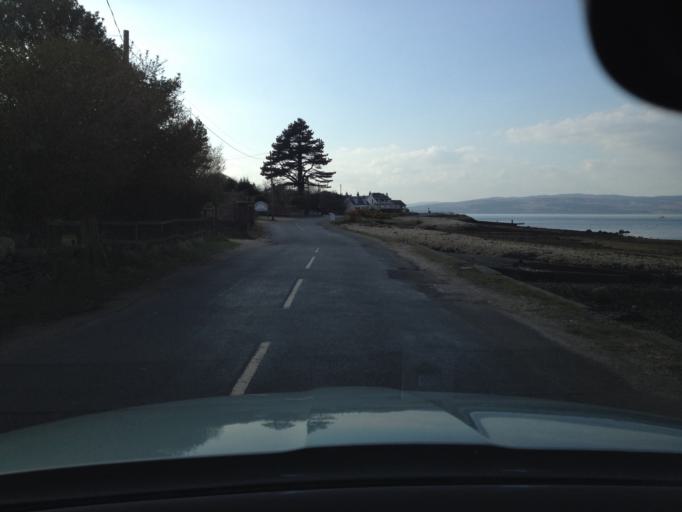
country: GB
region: Scotland
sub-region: North Ayrshire
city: Isle of Arran
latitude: 55.7053
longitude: -5.2960
